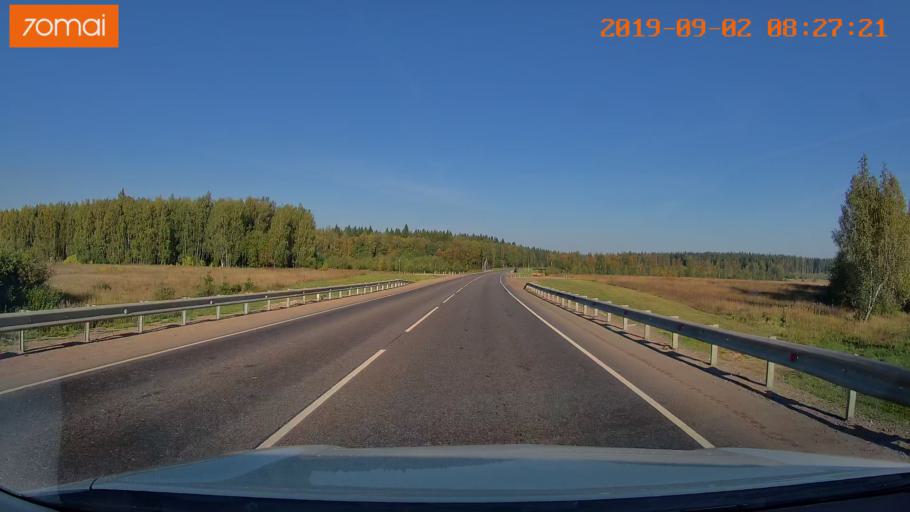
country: RU
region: Kaluga
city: Maloyaroslavets
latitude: 54.9812
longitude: 36.4186
